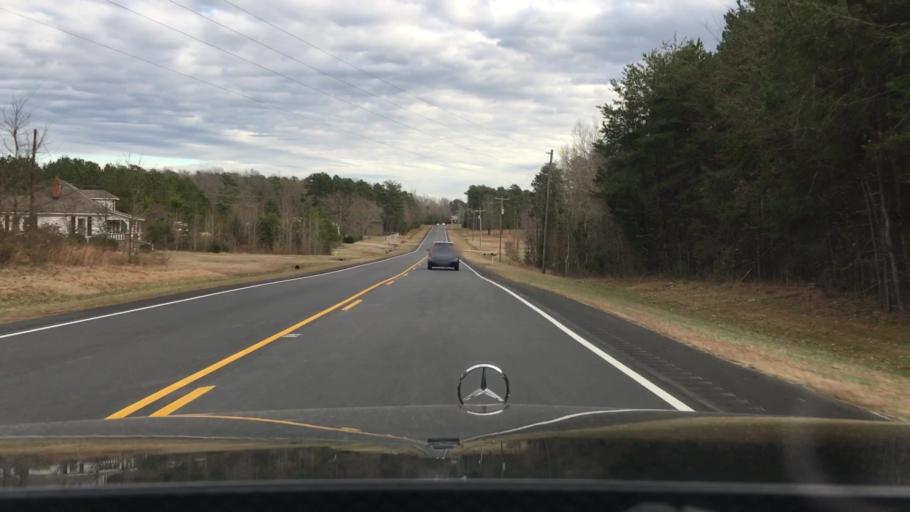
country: US
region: North Carolina
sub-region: Caswell County
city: Yanceyville
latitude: 36.2745
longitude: -79.2052
